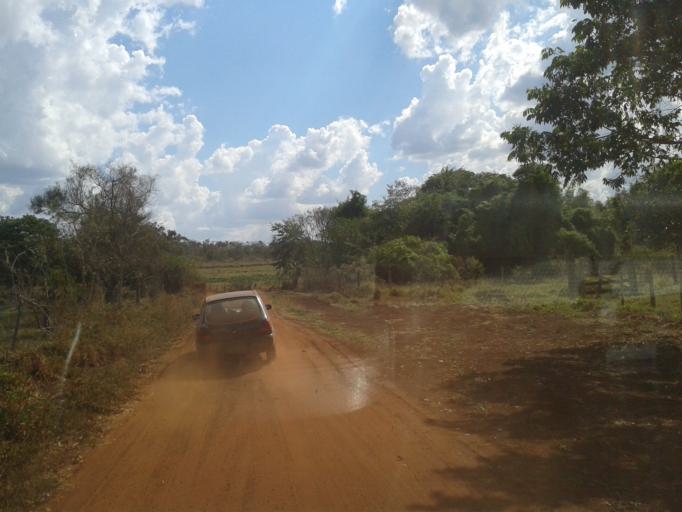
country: BR
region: Minas Gerais
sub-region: Santa Vitoria
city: Santa Vitoria
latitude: -19.1952
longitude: -49.9176
